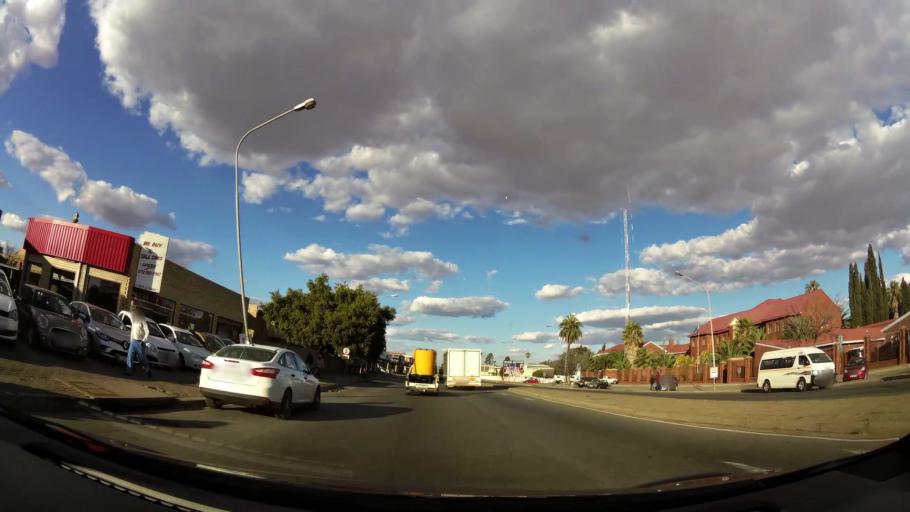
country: ZA
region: North-West
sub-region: Dr Kenneth Kaunda District Municipality
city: Potchefstroom
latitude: -26.7143
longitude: 27.0940
